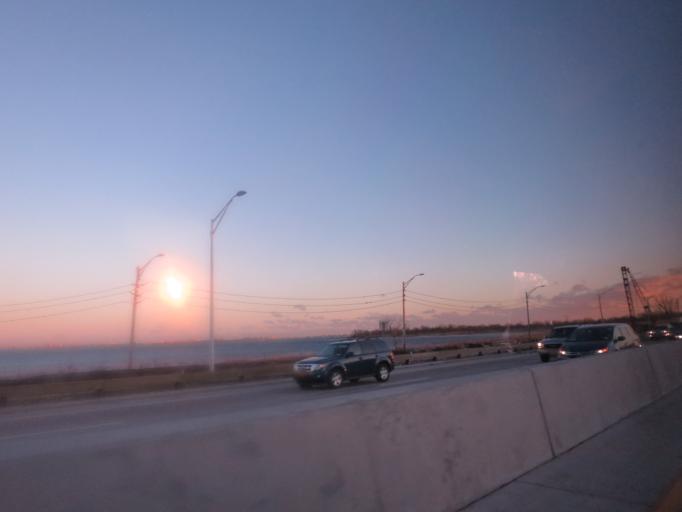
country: US
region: New York
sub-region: Kings County
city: East New York
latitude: 40.6169
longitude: -73.8973
